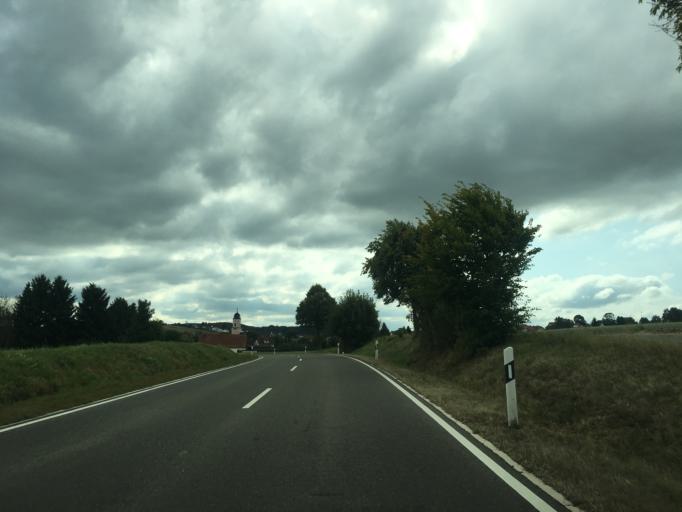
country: DE
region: Baden-Wuerttemberg
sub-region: Tuebingen Region
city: Sankt Johann
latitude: 48.3923
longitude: 9.2829
